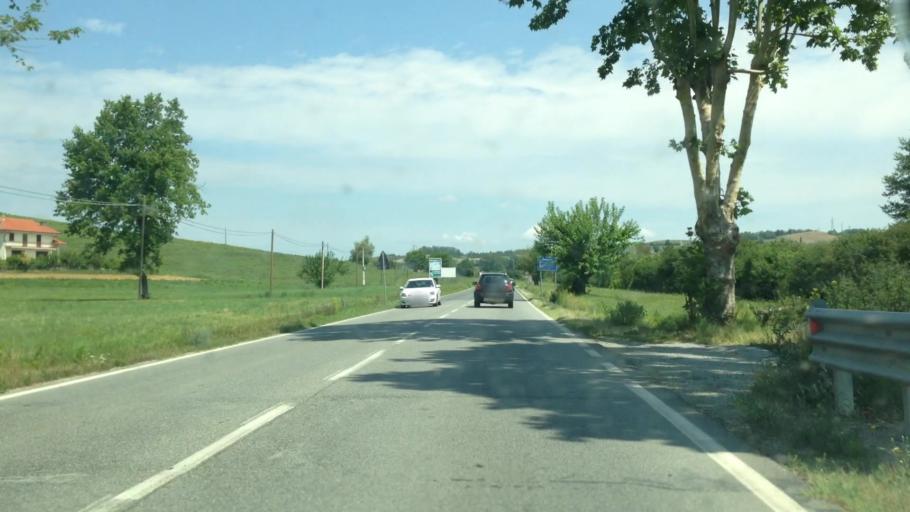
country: IT
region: Piedmont
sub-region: Provincia di Asti
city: Castell'Alfero
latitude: 44.9703
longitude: 8.2278
